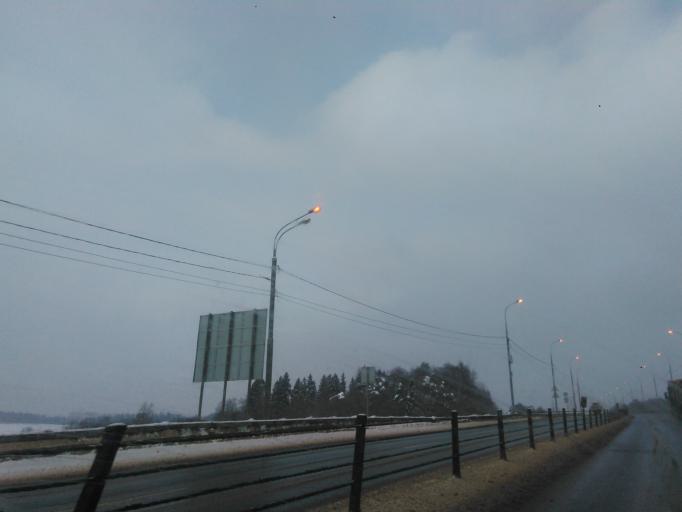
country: RU
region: Moskovskaya
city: Dedenevo
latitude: 56.2204
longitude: 37.5233
